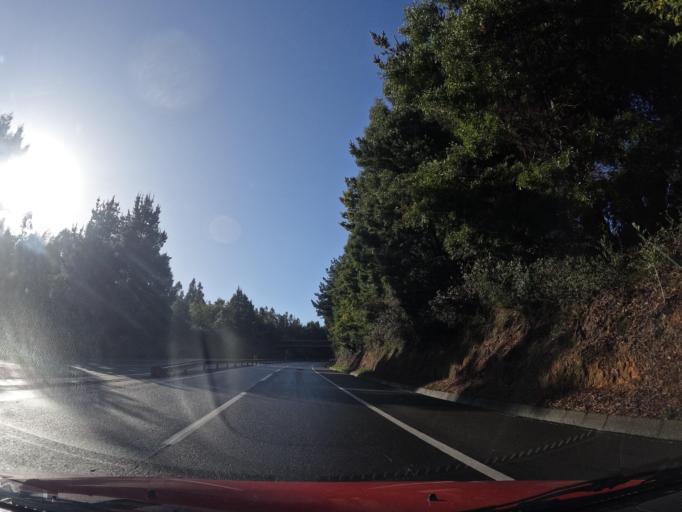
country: CL
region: Biobio
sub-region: Provincia de Concepcion
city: Penco
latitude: -36.7591
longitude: -72.9664
